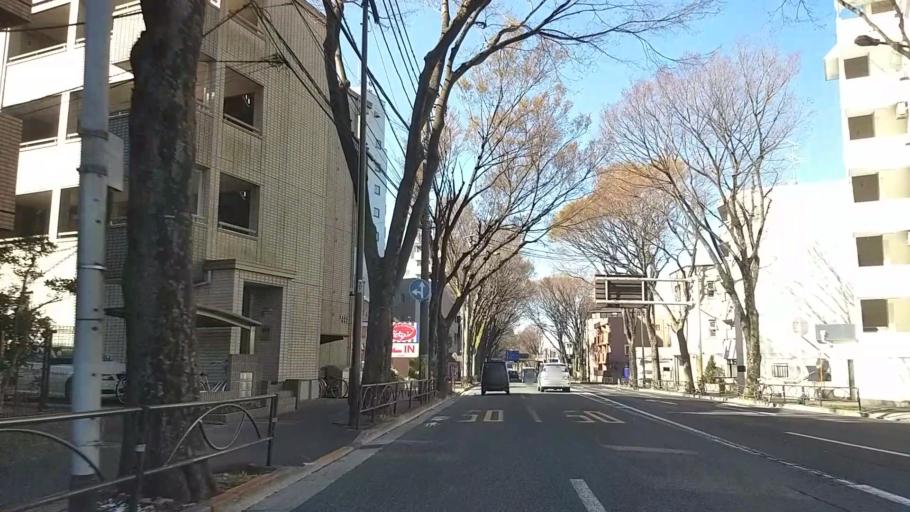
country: JP
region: Tokyo
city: Mitaka-shi
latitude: 35.6679
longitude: 139.5925
